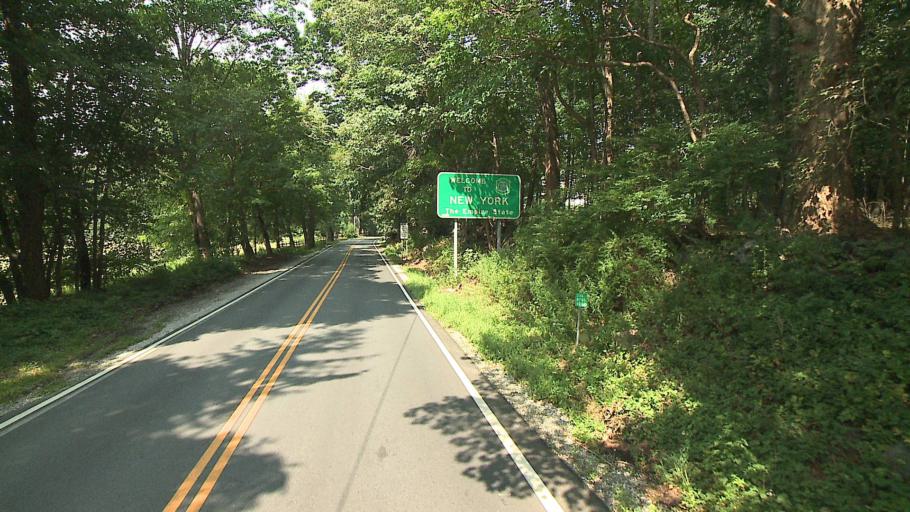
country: US
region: New York
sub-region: Putnam County
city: Peach Lake
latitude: 41.3289
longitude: -73.5470
